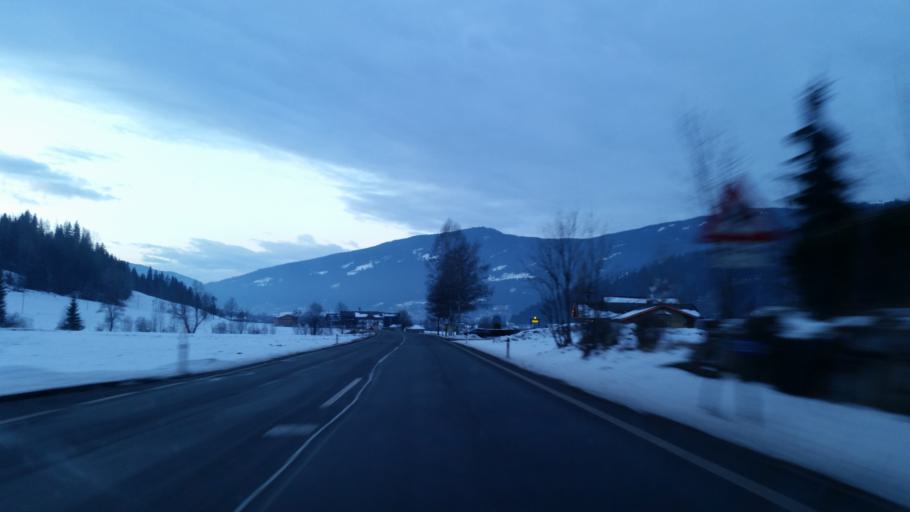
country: AT
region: Salzburg
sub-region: Politischer Bezirk Sankt Johann im Pongau
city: Forstau
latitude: 47.3624
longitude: 13.4930
